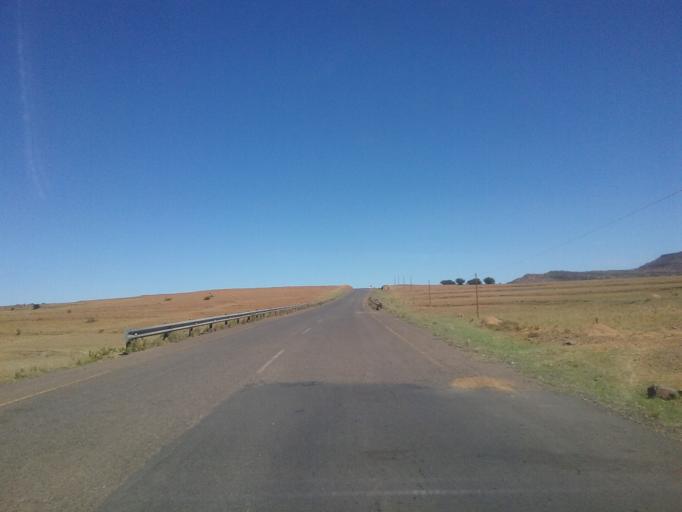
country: LS
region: Quthing
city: Quthing
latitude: -30.3813
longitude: 27.5832
